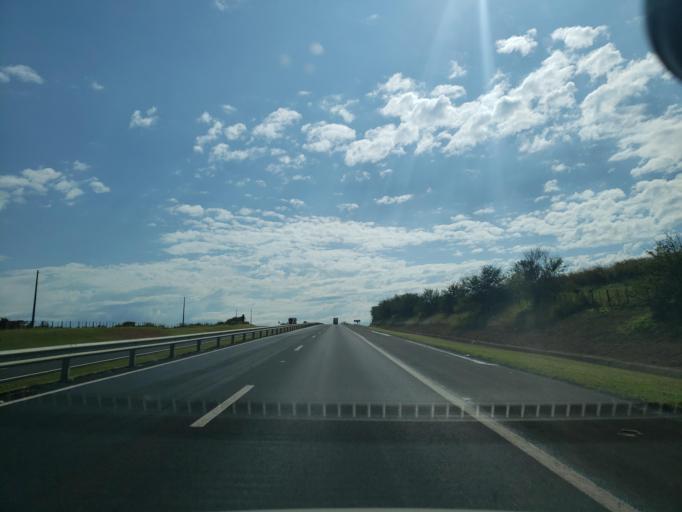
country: BR
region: Sao Paulo
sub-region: Pirajui
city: Pirajui
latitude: -22.0221
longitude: -49.4107
